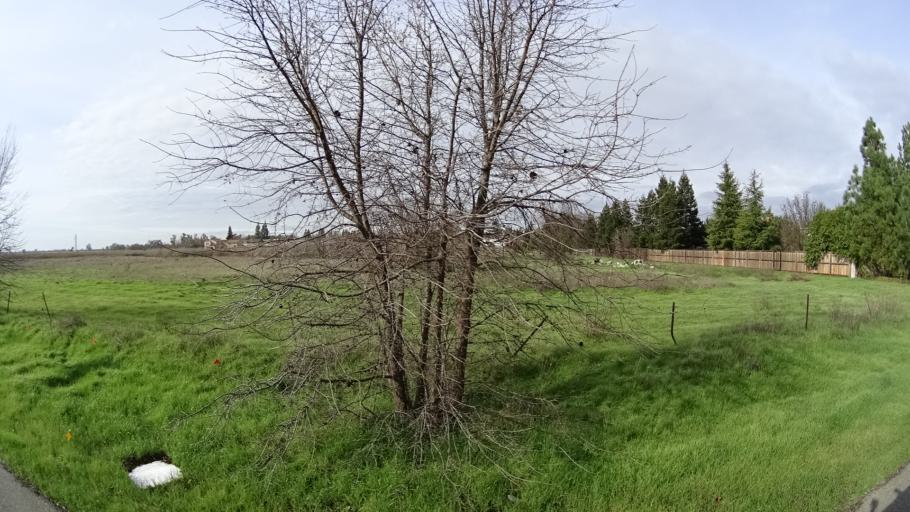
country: US
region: California
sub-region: Yolo County
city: Davis
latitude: 38.5405
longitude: -121.6946
